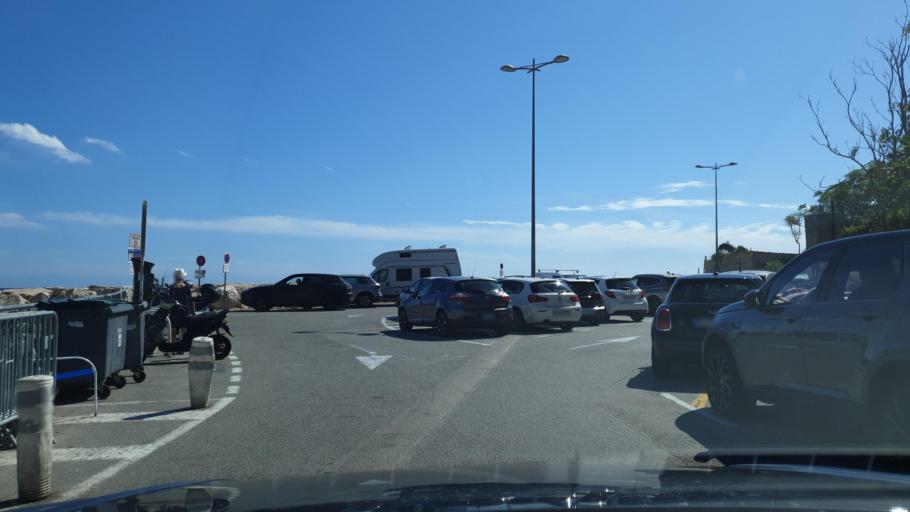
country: FR
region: Provence-Alpes-Cote d'Azur
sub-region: Departement des Alpes-Maritimes
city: Cap-d'Ail
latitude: 43.7231
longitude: 7.4107
